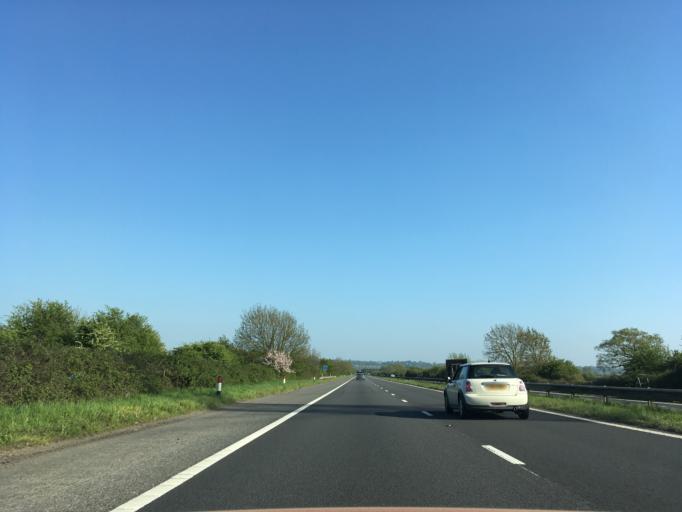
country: GB
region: England
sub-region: South Gloucestershire
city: Almondsbury
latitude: 51.5851
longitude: -2.5962
